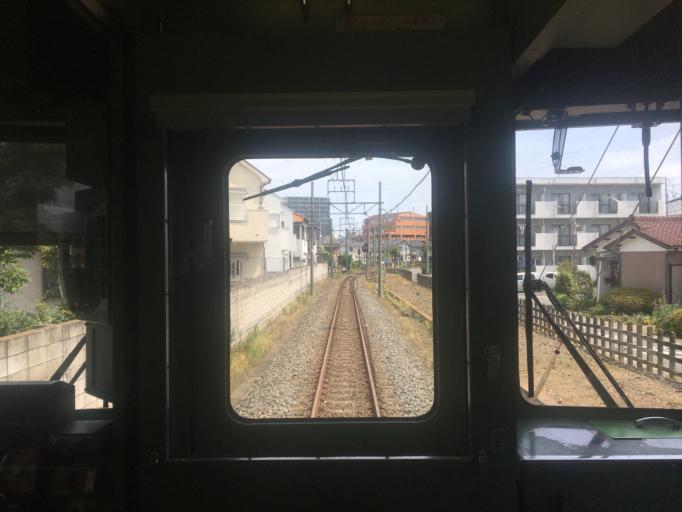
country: JP
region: Saitama
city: Sakado
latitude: 35.9549
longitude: 139.3902
